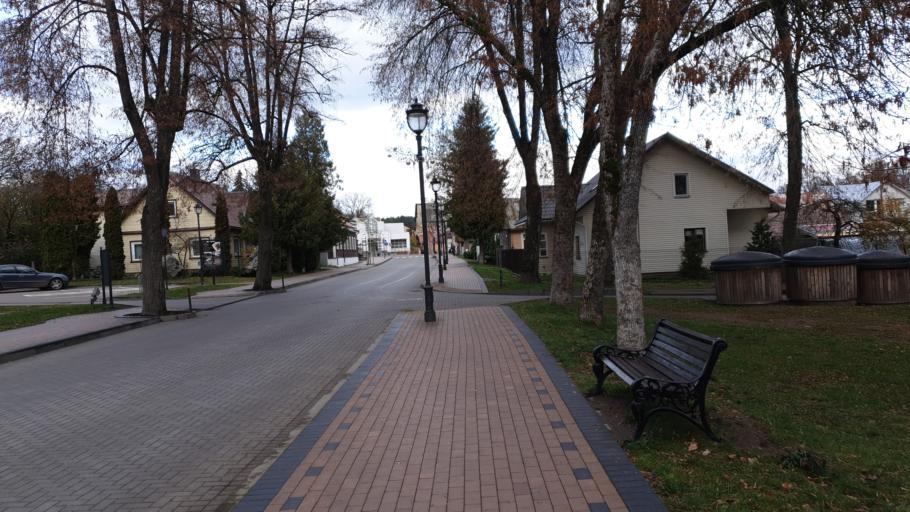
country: LT
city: Birstonas
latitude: 54.6021
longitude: 24.0344
